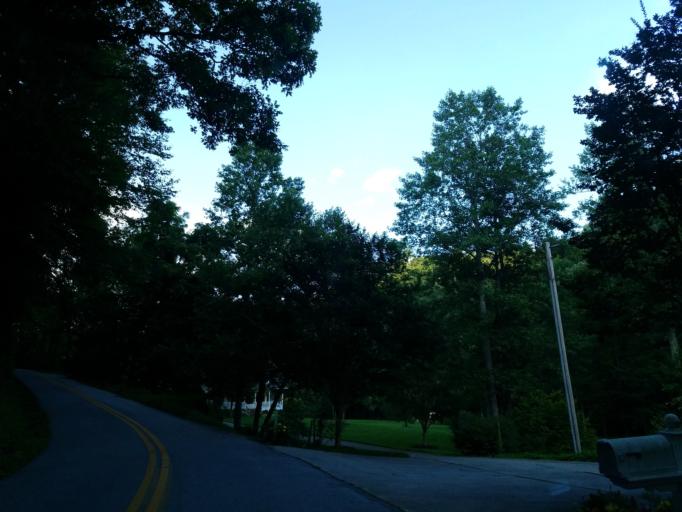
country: US
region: Georgia
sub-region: Lumpkin County
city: Dahlonega
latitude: 34.6765
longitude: -84.0781
